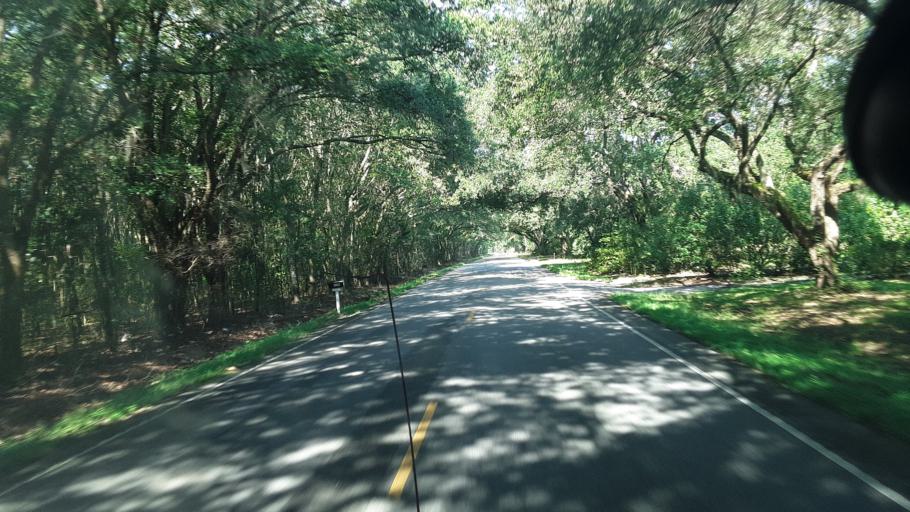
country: US
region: South Carolina
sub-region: Jasper County
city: Ridgeland
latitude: 32.5909
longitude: -80.9707
